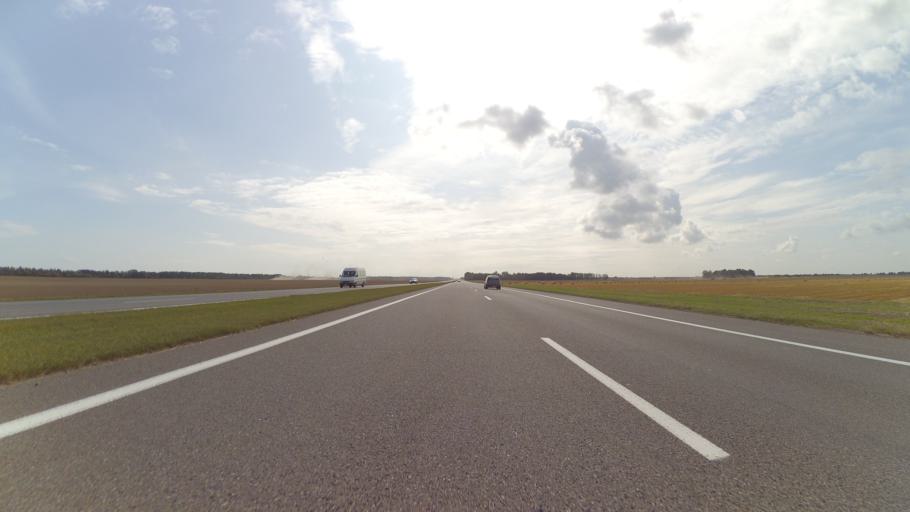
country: BY
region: Grodnenskaya
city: Skidal'
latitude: 53.6058
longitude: 24.1048
